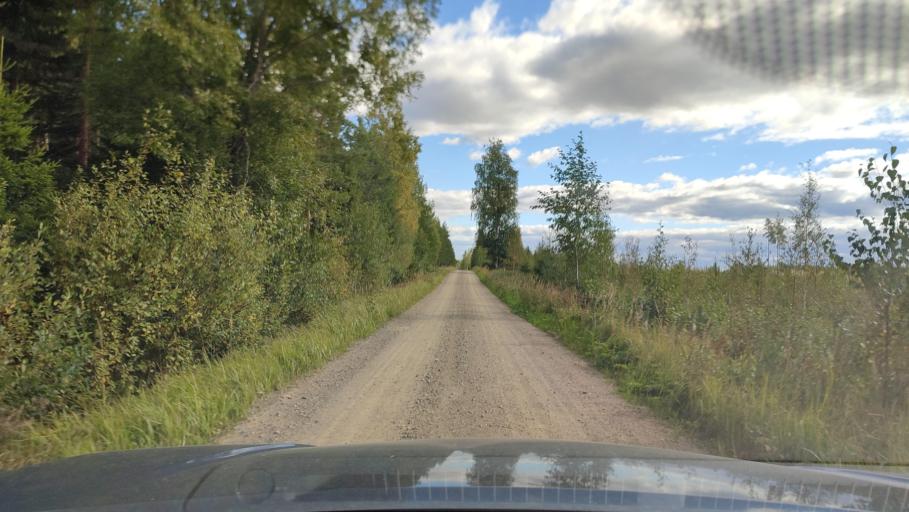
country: FI
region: Southern Ostrobothnia
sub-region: Suupohja
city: Karijoki
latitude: 62.2029
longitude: 21.6081
